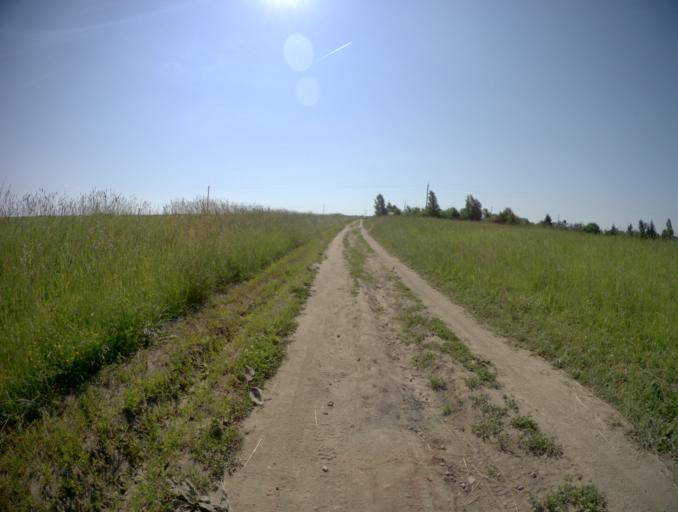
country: RU
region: Vladimir
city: Novovyazniki
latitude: 56.2347
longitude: 42.2469
